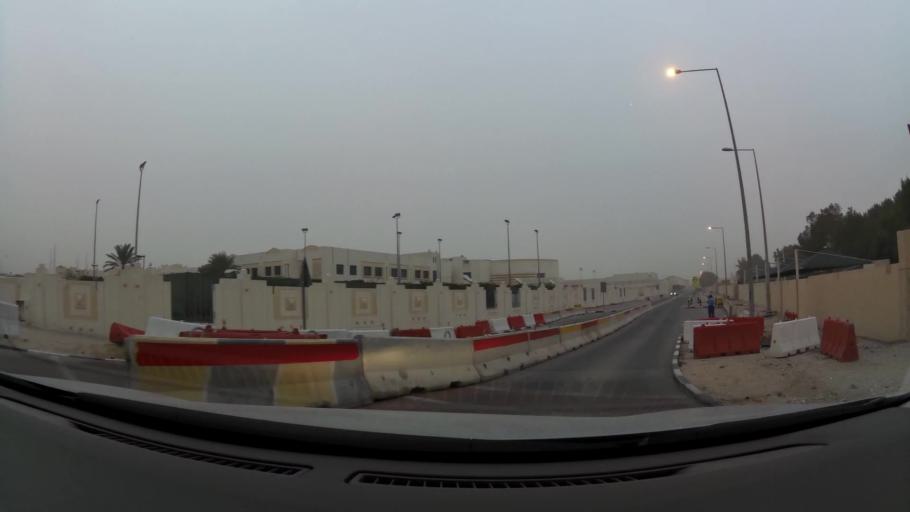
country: QA
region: Baladiyat ad Dawhah
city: Doha
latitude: 25.2319
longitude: 51.5034
